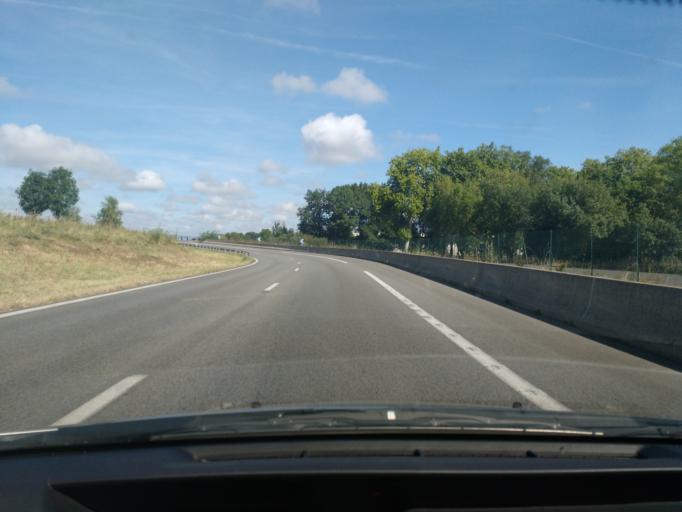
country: FR
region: Pays de la Loire
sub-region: Departement de Maine-et-Loire
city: Beaucouze
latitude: 47.4704
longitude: -0.6130
